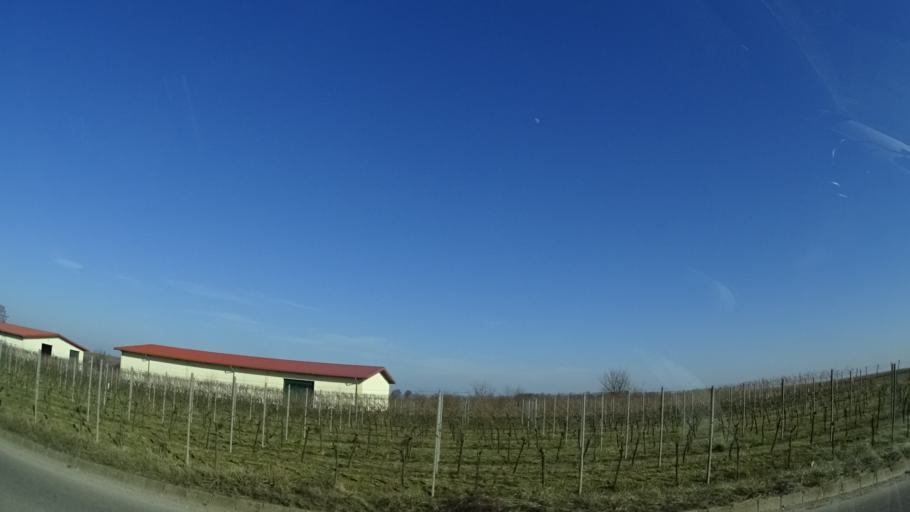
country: DE
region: Rheinland-Pfalz
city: Kirchheim an der Weinstrasse
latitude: 49.5343
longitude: 8.1804
